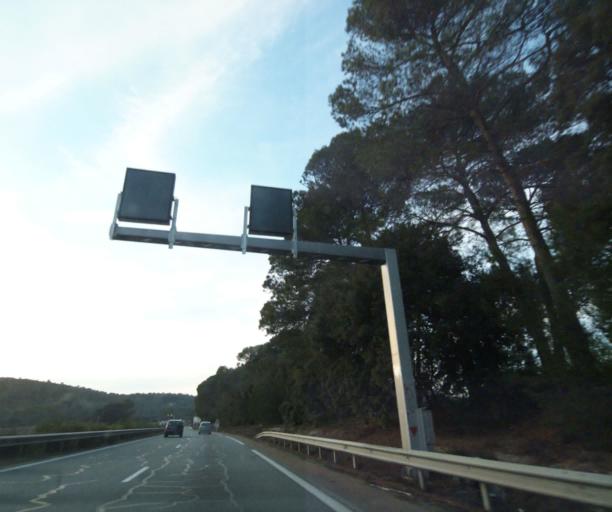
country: FR
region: Provence-Alpes-Cote d'Azur
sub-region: Departement du Var
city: La Motte
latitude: 43.4803
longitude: 6.5181
